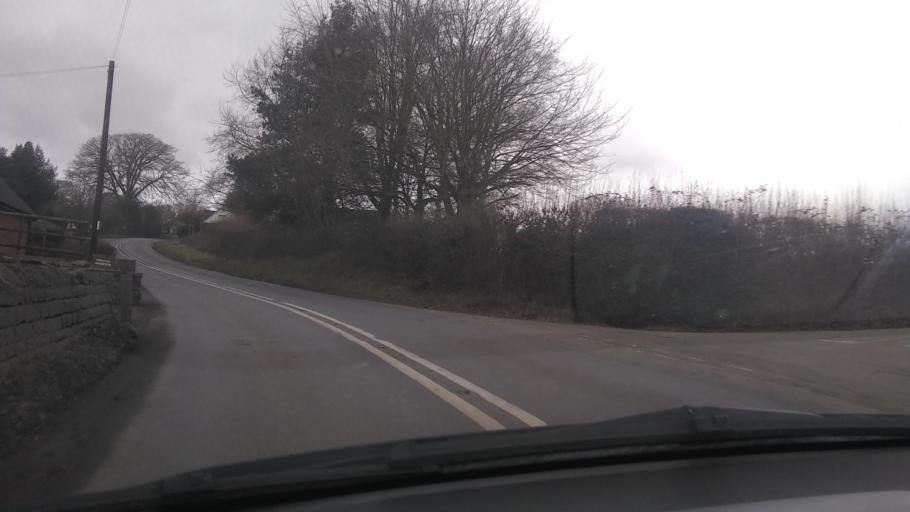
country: GB
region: England
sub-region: Shropshire
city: Cleobury Mortimer
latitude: 52.3832
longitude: -2.5343
